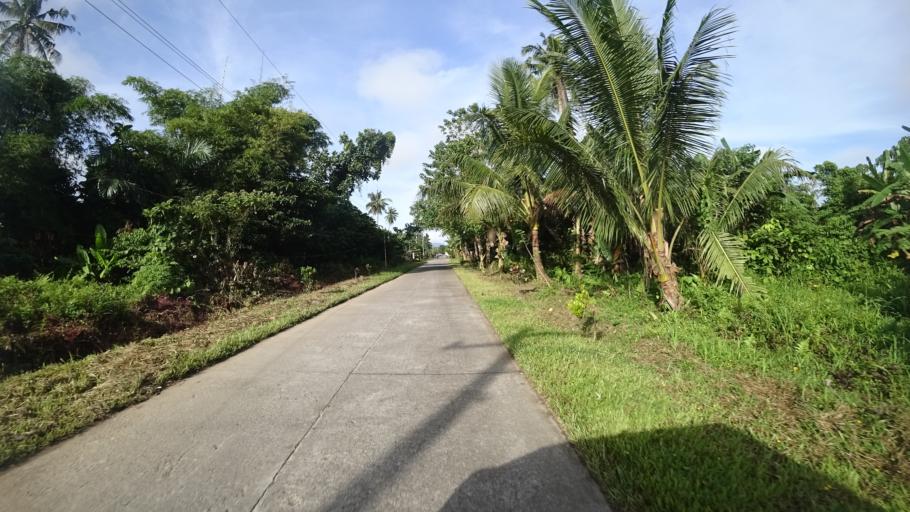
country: PH
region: Eastern Visayas
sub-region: Province of Leyte
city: Alangalang
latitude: 11.1849
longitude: 124.8738
